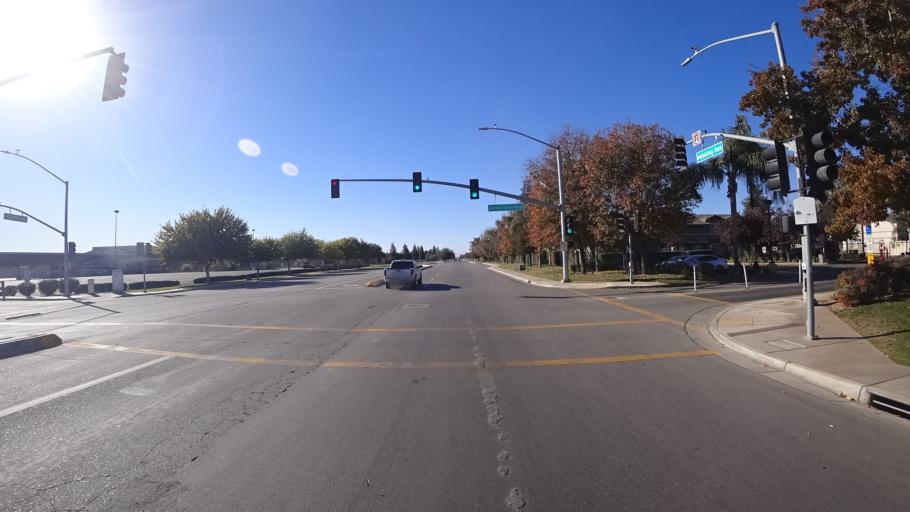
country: US
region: California
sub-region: Kern County
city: Greenfield
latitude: 35.2814
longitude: -119.0077
